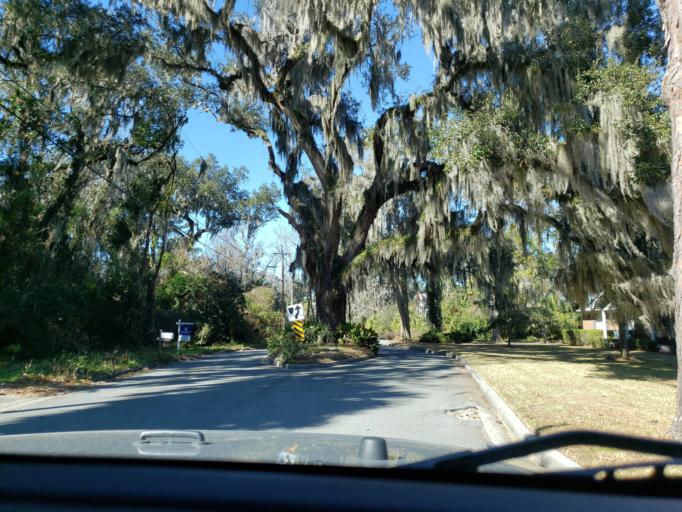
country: US
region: Georgia
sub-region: Chatham County
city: Whitemarsh Island
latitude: 32.0389
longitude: -80.9875
